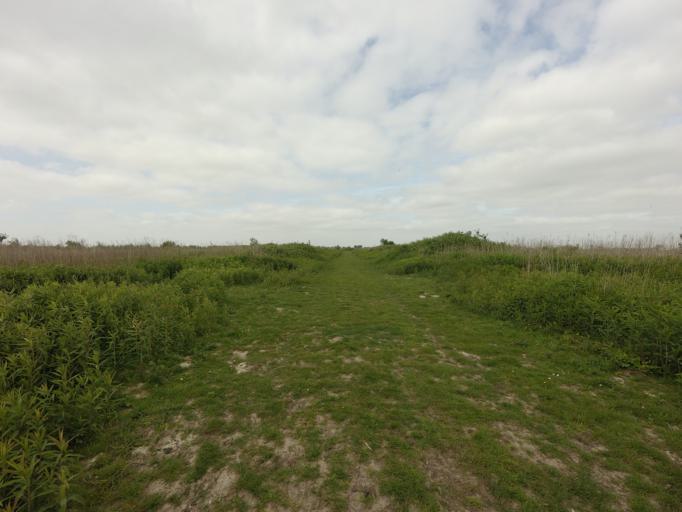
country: NL
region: North Brabant
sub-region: Gemeente Steenbergen
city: Dinteloord
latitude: 51.7304
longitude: 4.3338
